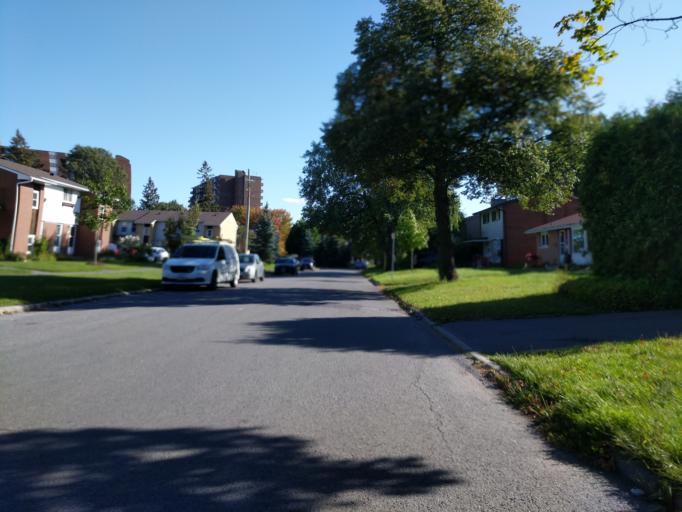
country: CA
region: Ontario
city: Ottawa
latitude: 45.3633
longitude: -75.7442
